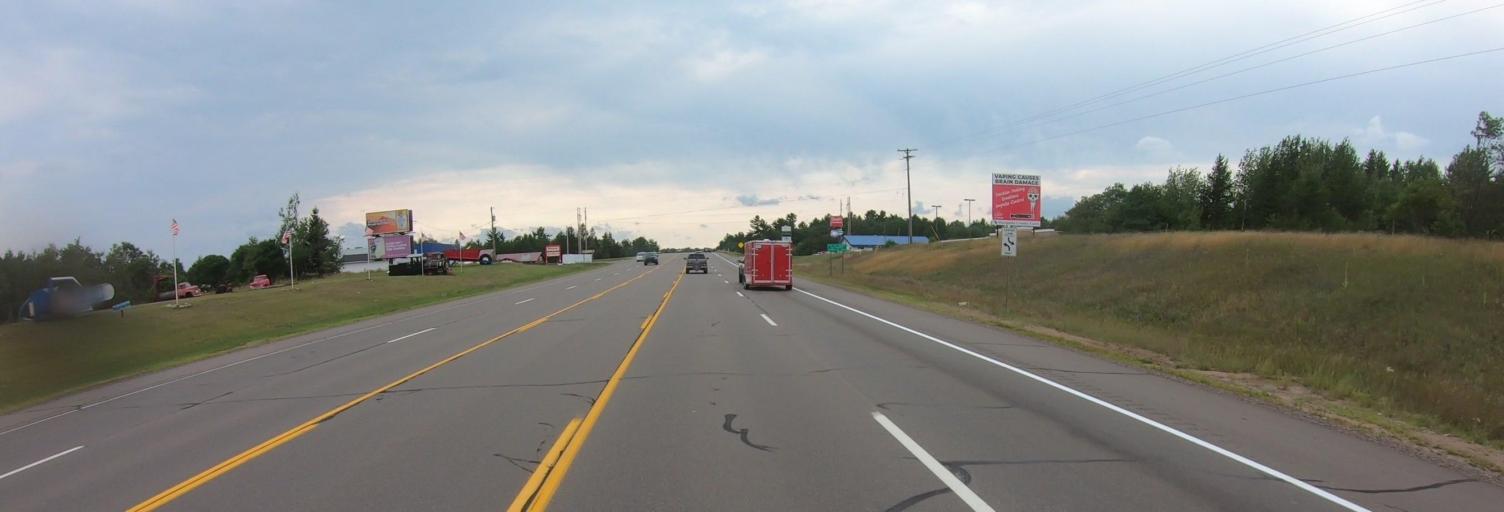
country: US
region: Michigan
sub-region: Marquette County
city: West Ishpeming
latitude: 46.4931
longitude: -87.6982
